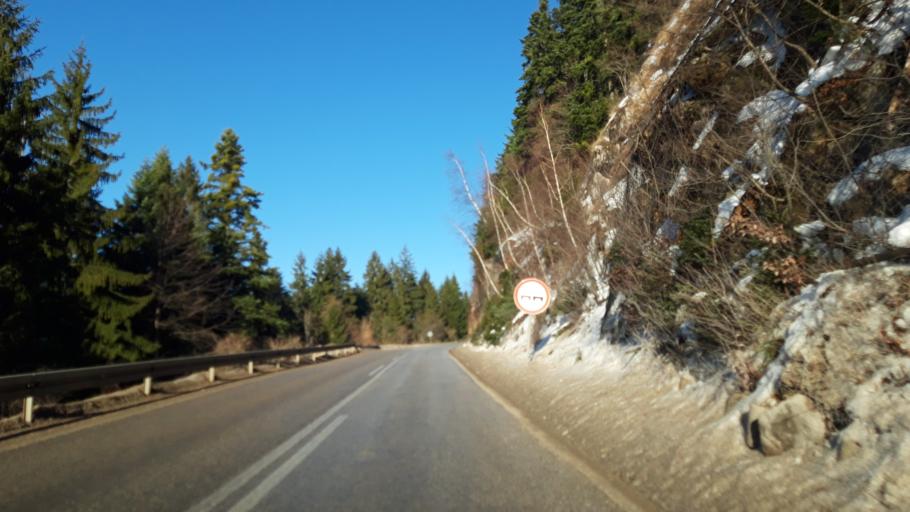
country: BA
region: Republika Srpska
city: Pale
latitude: 43.9090
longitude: 18.6389
